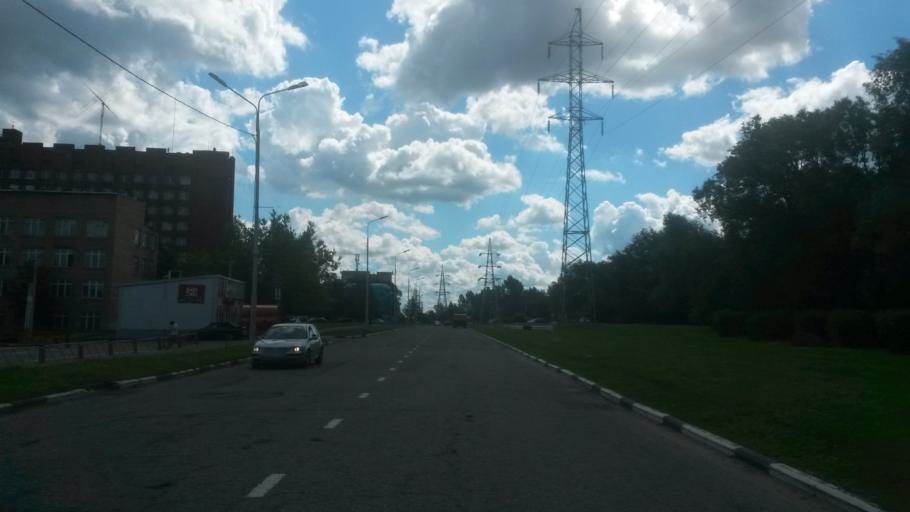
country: RU
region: Jaroslavl
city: Yaroslavl
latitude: 57.5866
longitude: 39.8518
